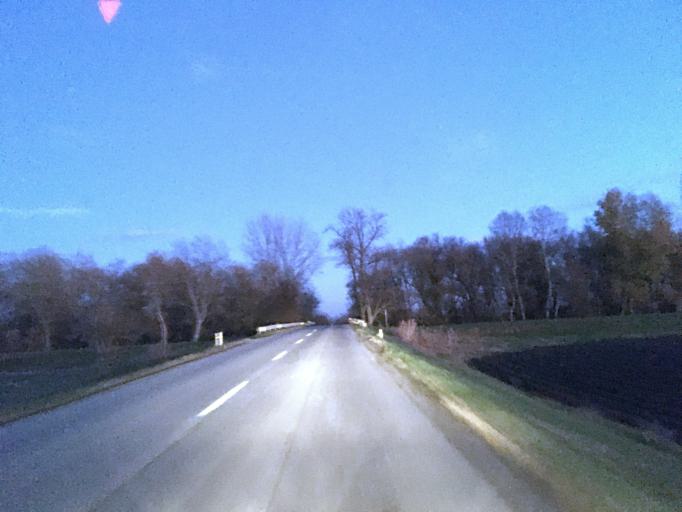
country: SK
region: Nitriansky
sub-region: Okres Komarno
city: Hurbanovo
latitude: 47.8949
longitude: 18.1846
